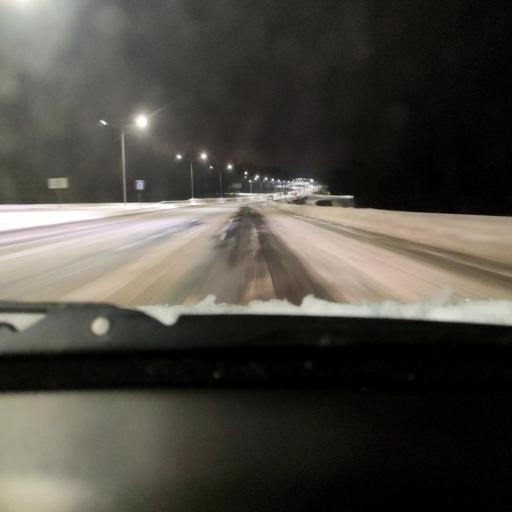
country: RU
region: Perm
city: Novyye Lyady
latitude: 58.0851
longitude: 56.4295
